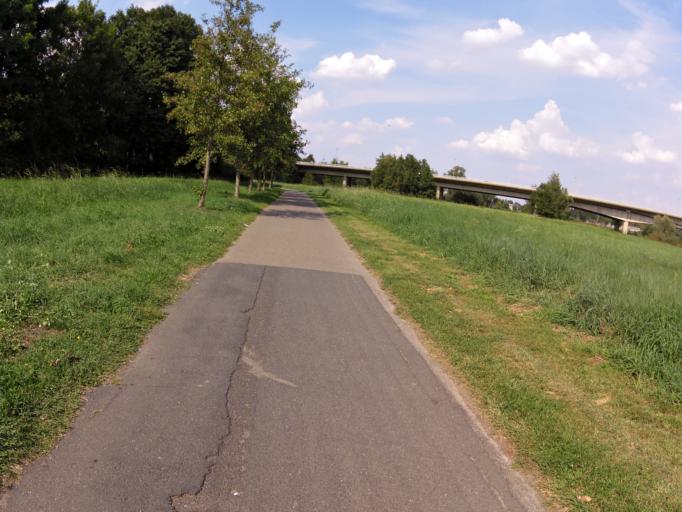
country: DE
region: North Rhine-Westphalia
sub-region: Regierungsbezirk Detmold
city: Minden
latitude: 52.2962
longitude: 8.9279
